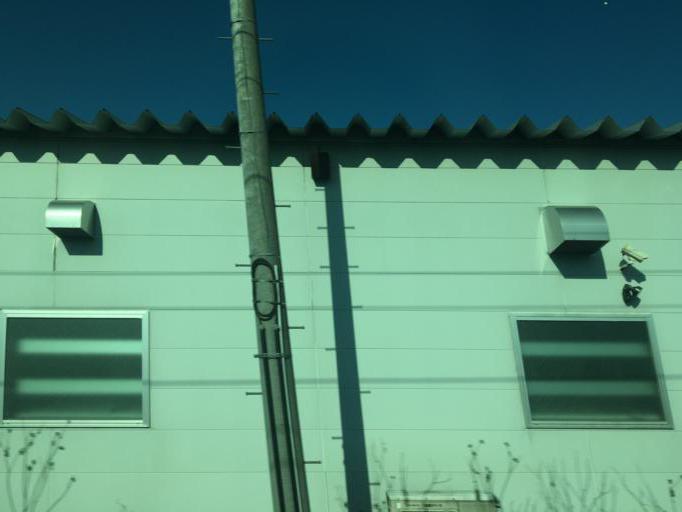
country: JP
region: Ibaraki
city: Iwase
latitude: 36.3578
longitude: 140.1229
